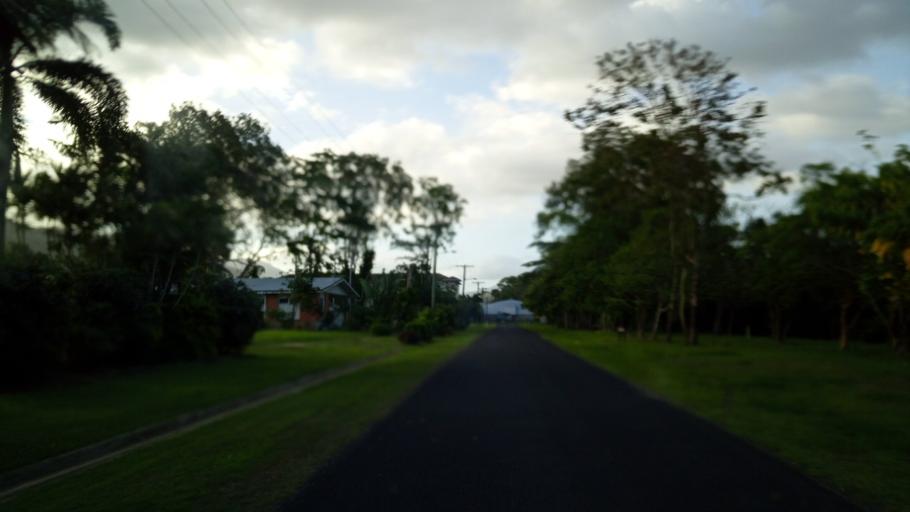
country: AU
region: Queensland
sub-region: Cairns
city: Woree
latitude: -16.9345
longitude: 145.7454
